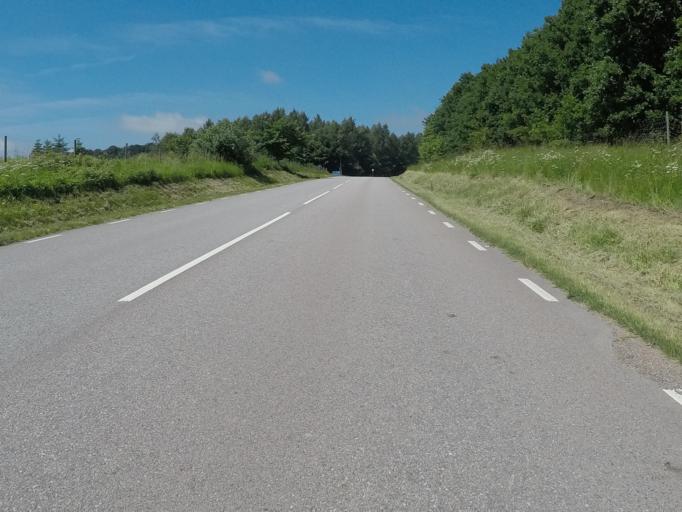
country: SE
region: Skane
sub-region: Malmo
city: Oxie
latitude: 55.5291
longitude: 13.1416
